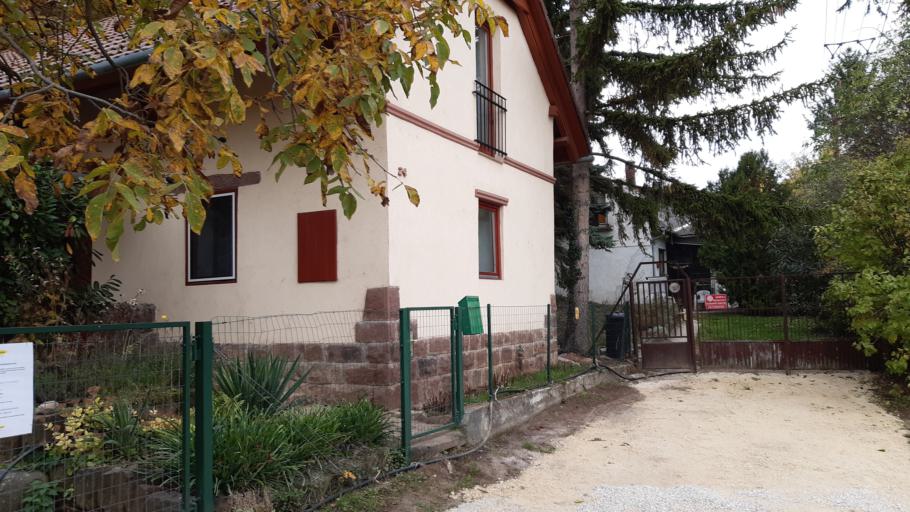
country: HU
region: Veszprem
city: Balatonalmadi
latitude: 47.0459
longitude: 18.0017
